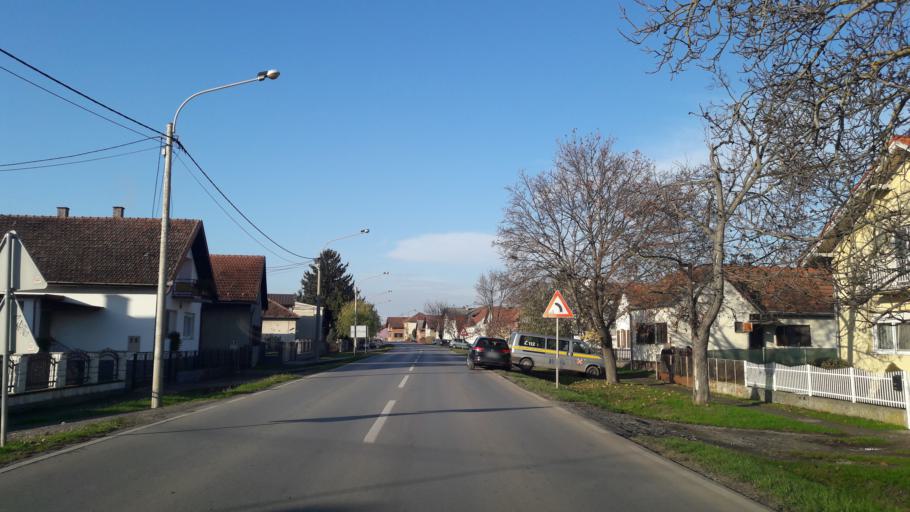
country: HR
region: Osjecko-Baranjska
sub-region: Grad Osijek
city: Bilje
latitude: 45.6062
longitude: 18.7428
